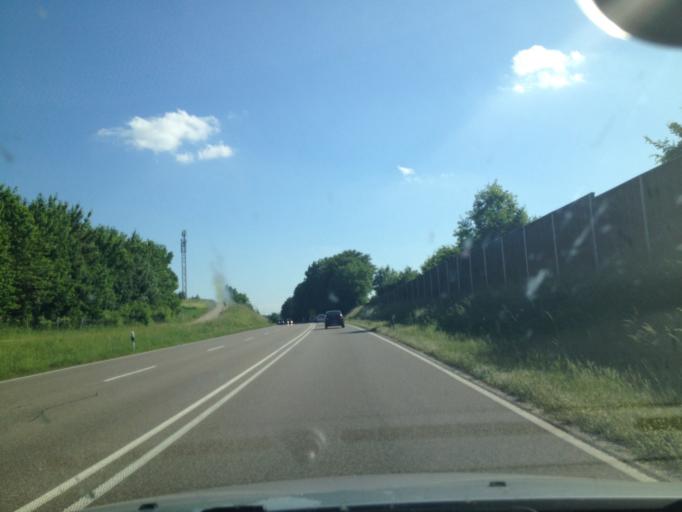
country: DE
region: Bavaria
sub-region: Swabia
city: Aichach
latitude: 48.4509
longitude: 11.1440
